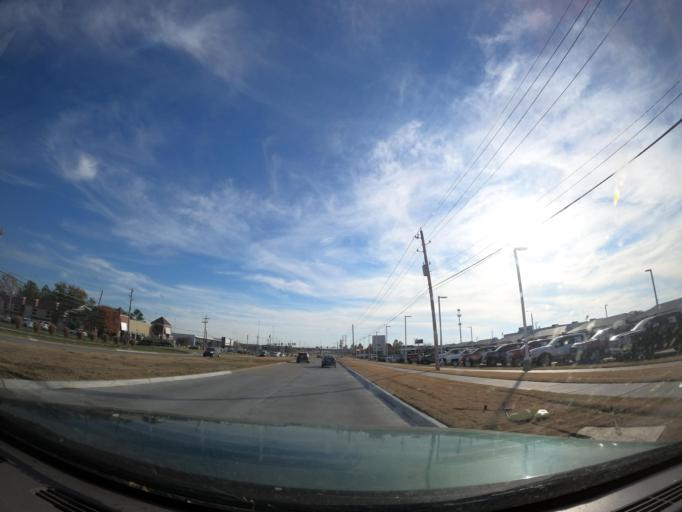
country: US
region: Oklahoma
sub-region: Tulsa County
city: Jenks
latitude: 36.0296
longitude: -95.8865
